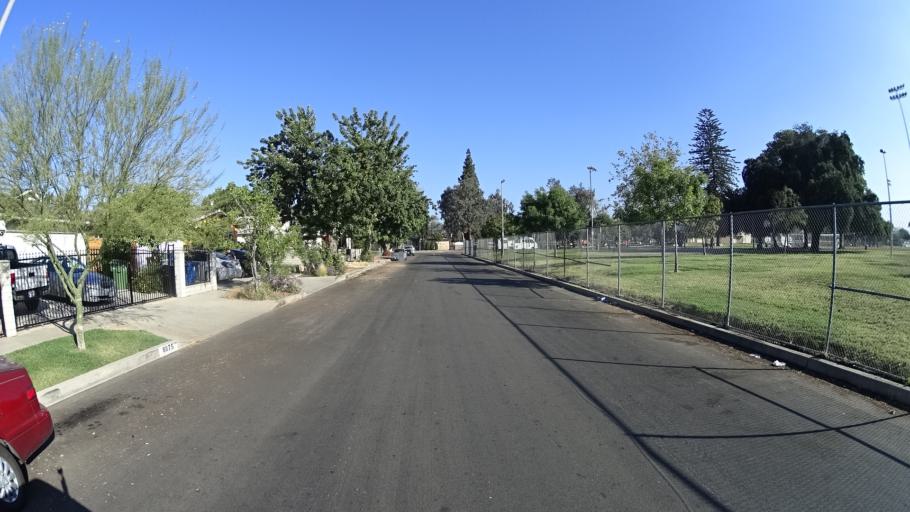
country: US
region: California
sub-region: Los Angeles County
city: Van Nuys
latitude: 34.2311
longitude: -118.4236
